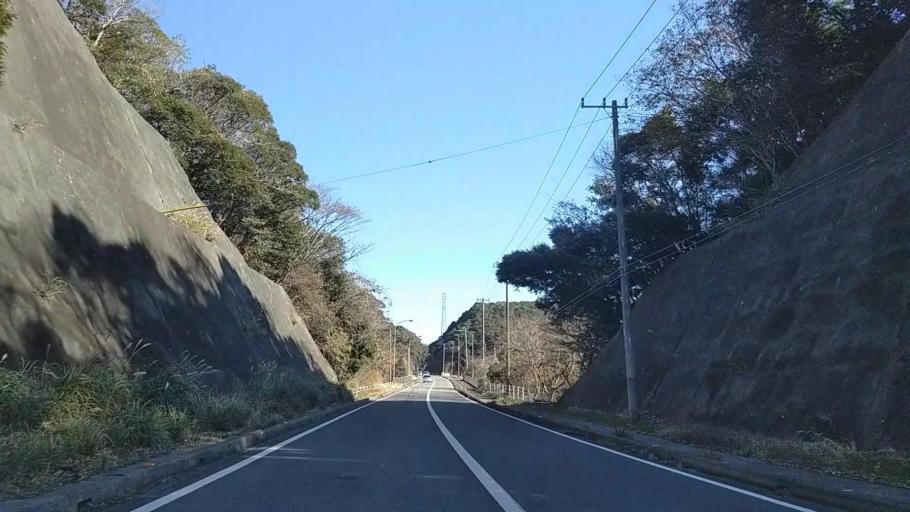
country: JP
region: Chiba
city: Katsuura
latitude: 35.1404
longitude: 140.2514
